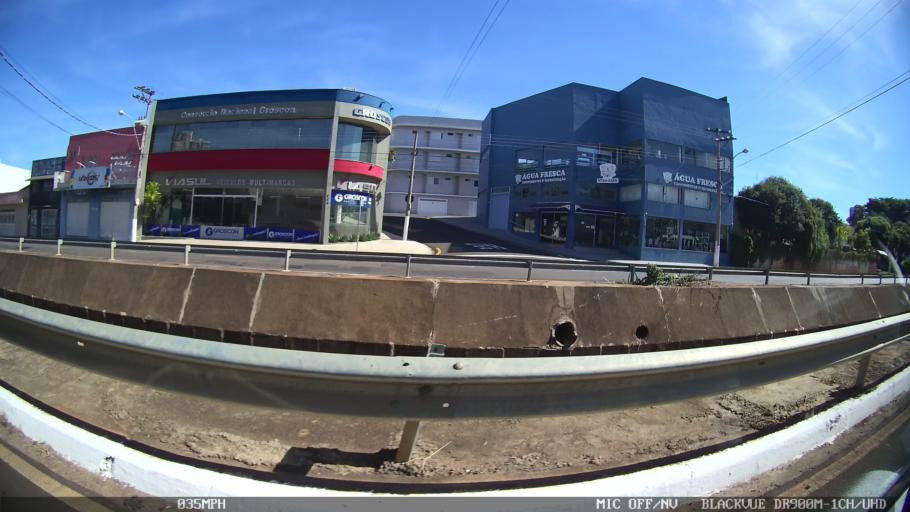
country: BR
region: Sao Paulo
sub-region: Franca
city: Franca
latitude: -20.5436
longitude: -47.4083
